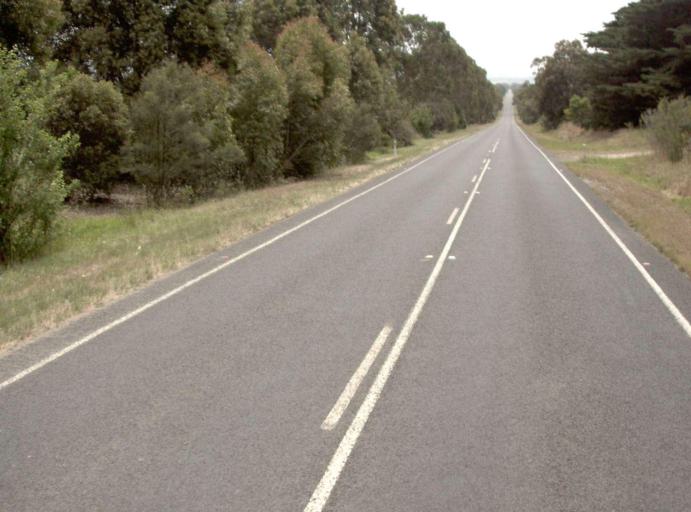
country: AU
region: Victoria
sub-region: Latrobe
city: Traralgon
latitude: -38.5064
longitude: 146.7099
